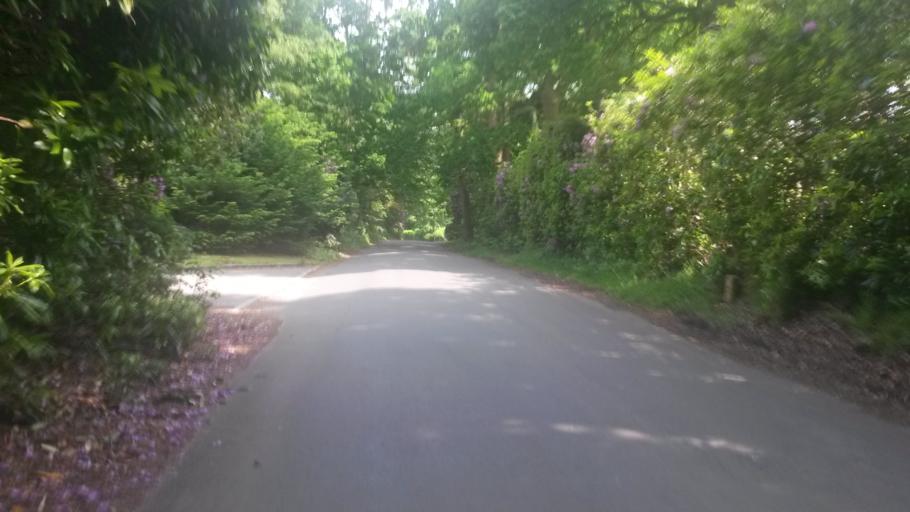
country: GB
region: England
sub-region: Surrey
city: Haslemere
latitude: 51.0791
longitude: -0.7011
